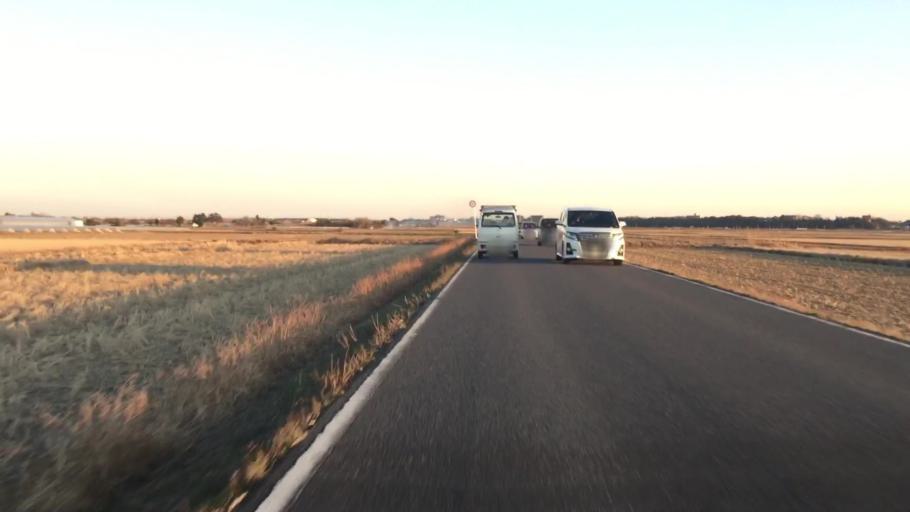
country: JP
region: Chiba
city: Abiko
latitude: 35.8965
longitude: 140.0197
